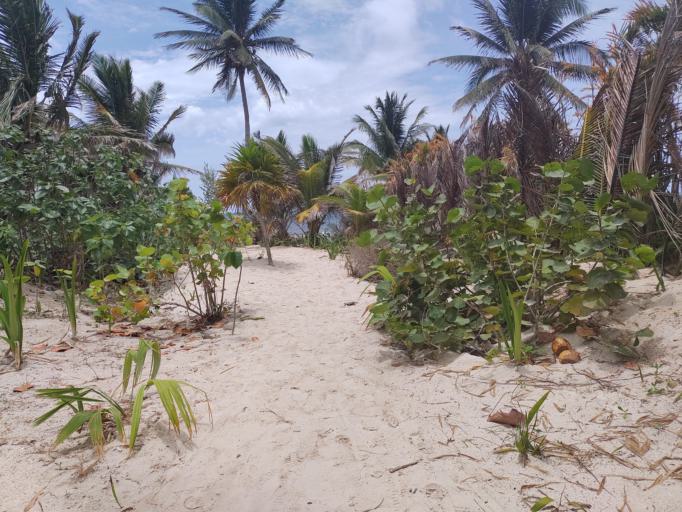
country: MX
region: Quintana Roo
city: Tulum
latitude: 20.2084
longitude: -87.4311
